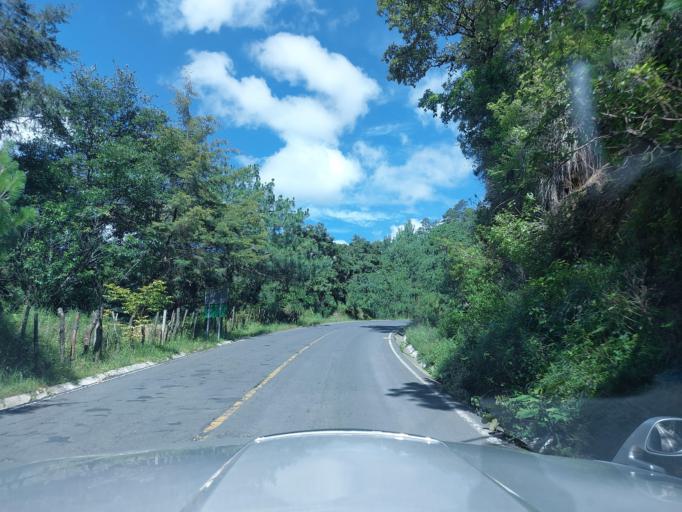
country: GT
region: Chimaltenango
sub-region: Municipio de Santa Cruz Balanya
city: Santa Cruz Balanya
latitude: 14.6963
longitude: -90.8960
